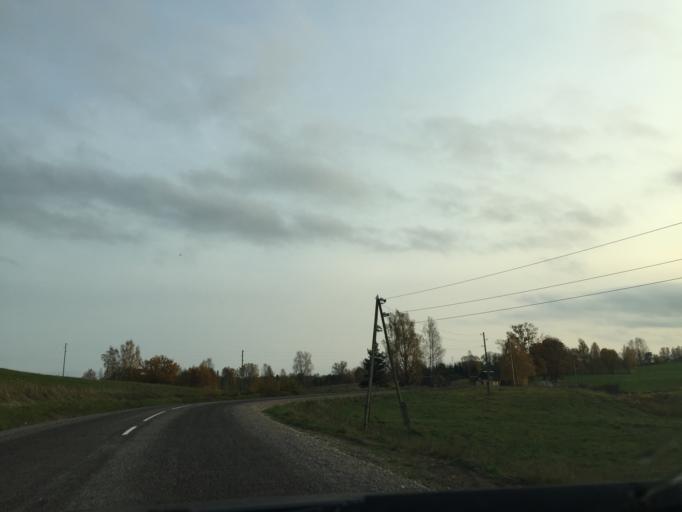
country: LV
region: Pargaujas
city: Stalbe
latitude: 57.3233
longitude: 25.1404
